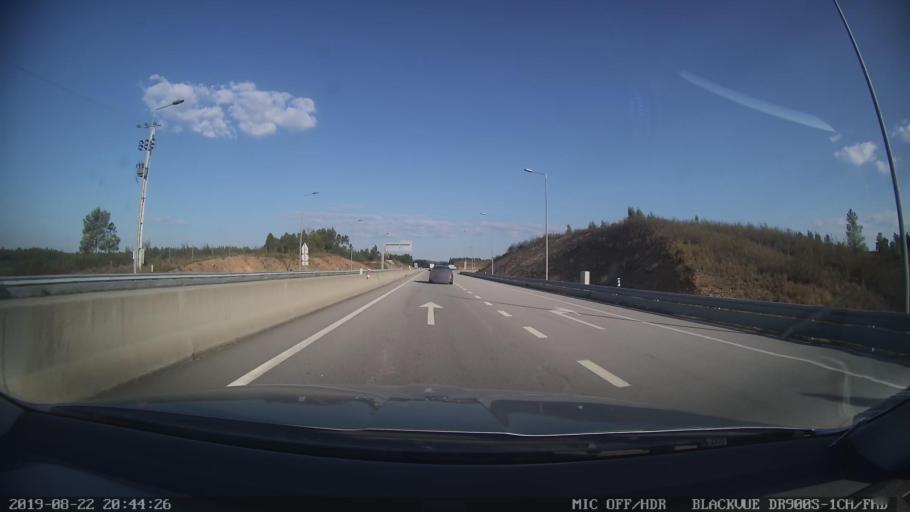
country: PT
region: Castelo Branco
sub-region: Proenca-A-Nova
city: Proenca-a-Nova
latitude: 39.7074
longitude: -7.8514
